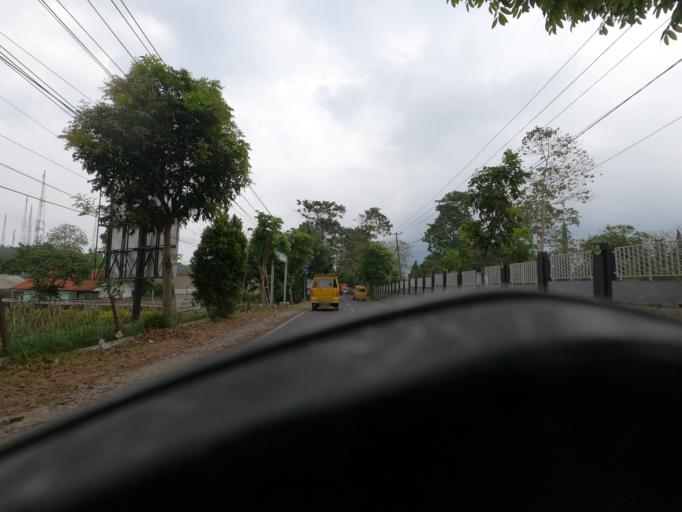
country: ID
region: West Java
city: Lembang
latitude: -6.8106
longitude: 107.5655
